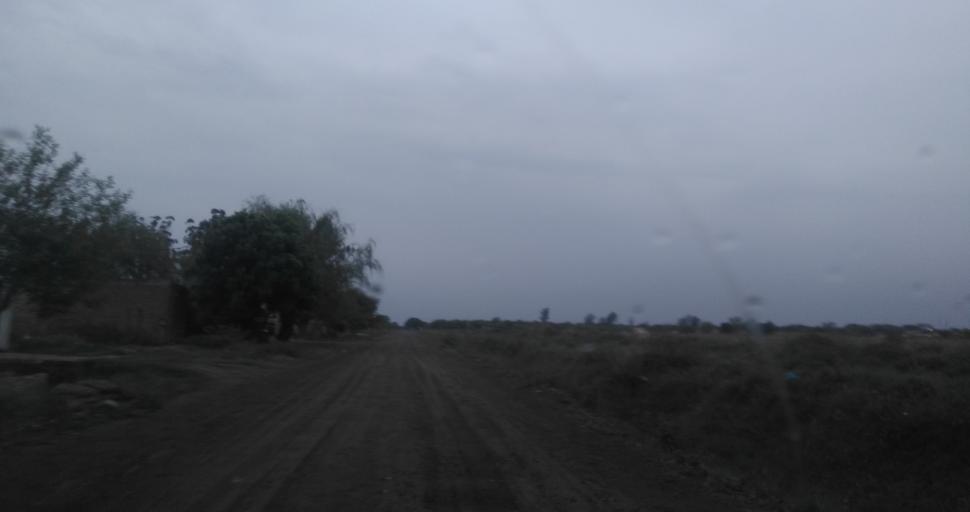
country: AR
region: Chaco
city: Fontana
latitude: -27.4211
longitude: -59.0408
